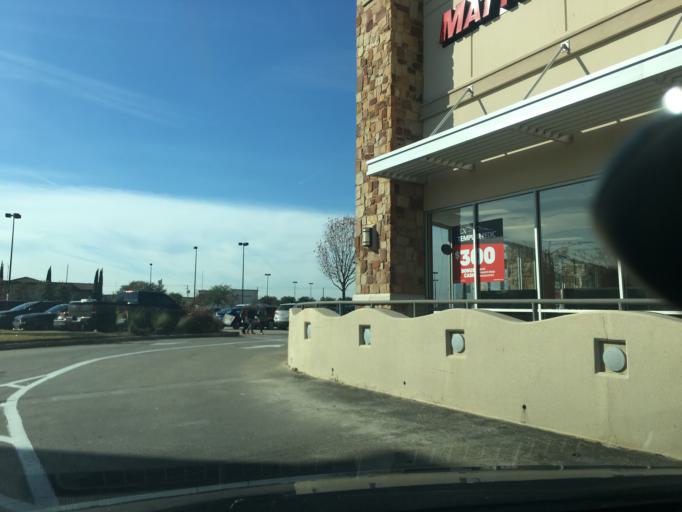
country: US
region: Texas
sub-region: Harris County
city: Cloverleaf
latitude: 29.8099
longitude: -95.1602
